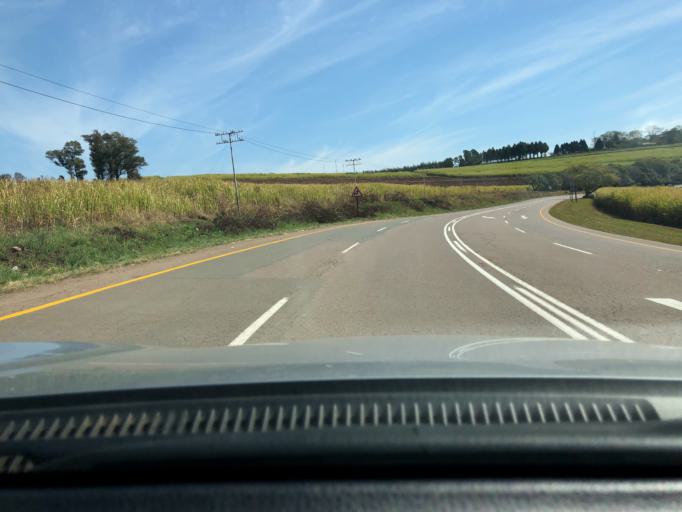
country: ZA
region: KwaZulu-Natal
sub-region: uMgungundlovu District Municipality
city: Richmond
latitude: -29.8210
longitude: 30.3437
